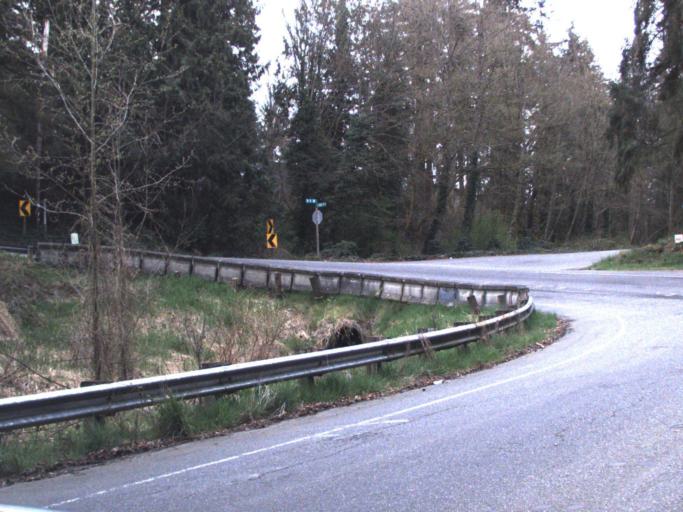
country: US
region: Washington
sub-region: King County
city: Federal Way
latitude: 47.3197
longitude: -122.3658
